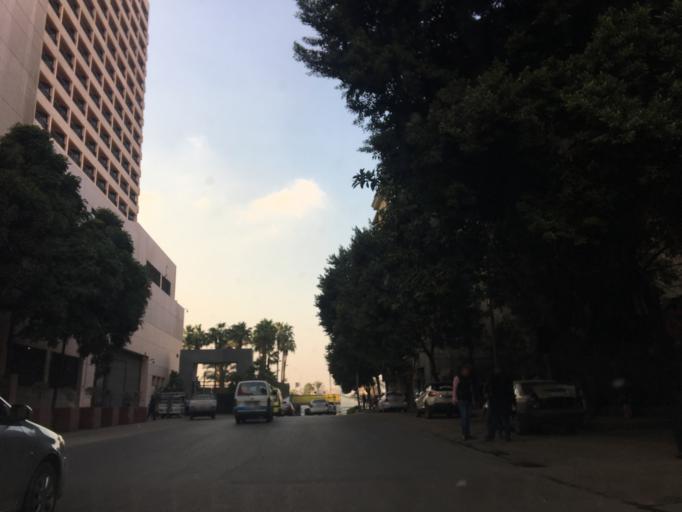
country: EG
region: Muhafazat al Qahirah
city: Cairo
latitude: 30.0428
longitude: 31.2329
